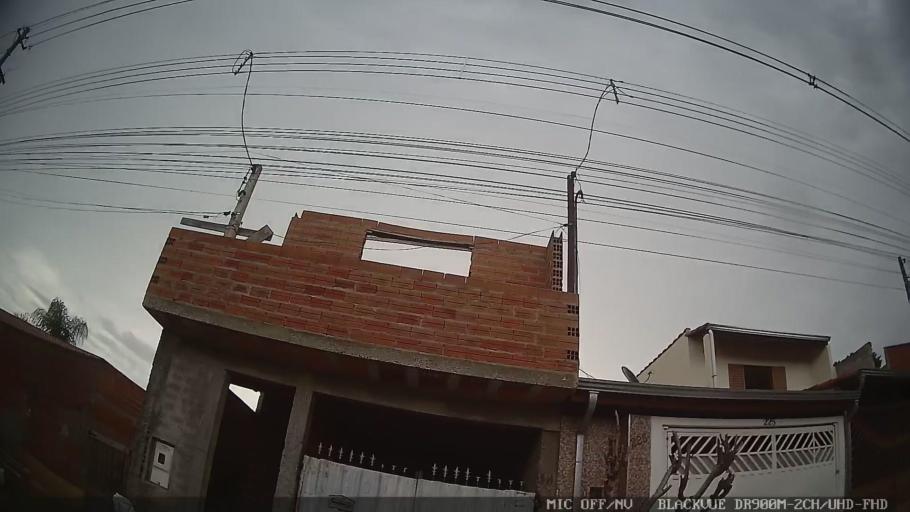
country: BR
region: Sao Paulo
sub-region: Pedreira
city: Pedreira
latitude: -22.7132
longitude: -46.8972
